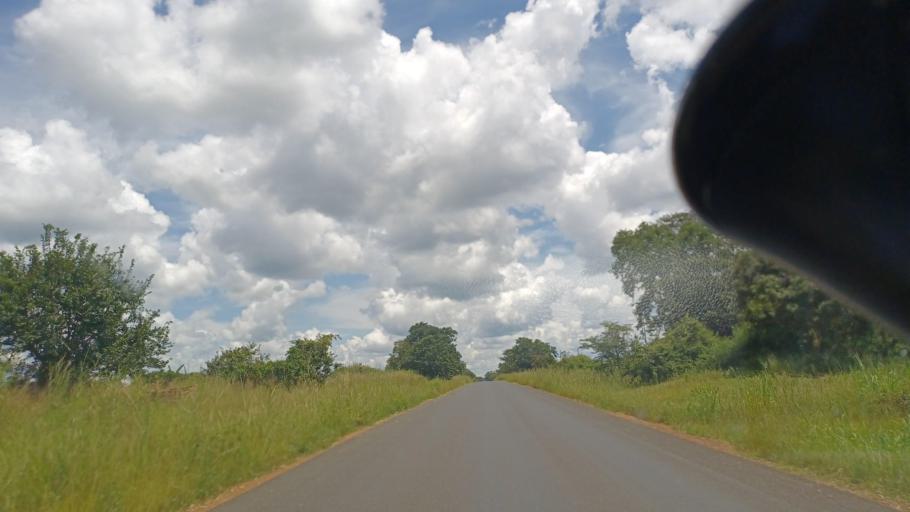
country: ZM
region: North-Western
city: Solwezi
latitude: -12.4077
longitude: 26.2387
